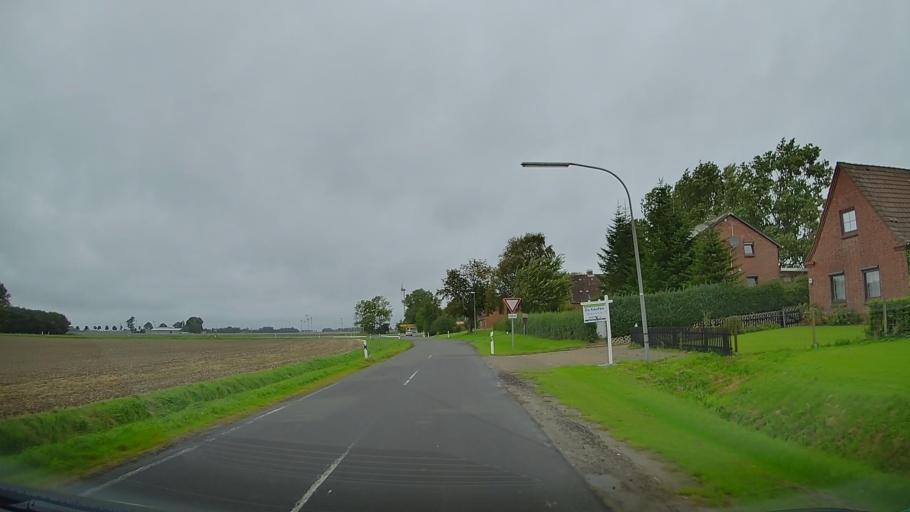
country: DE
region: Schleswig-Holstein
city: Marnerdeich
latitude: 53.9297
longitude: 8.9823
